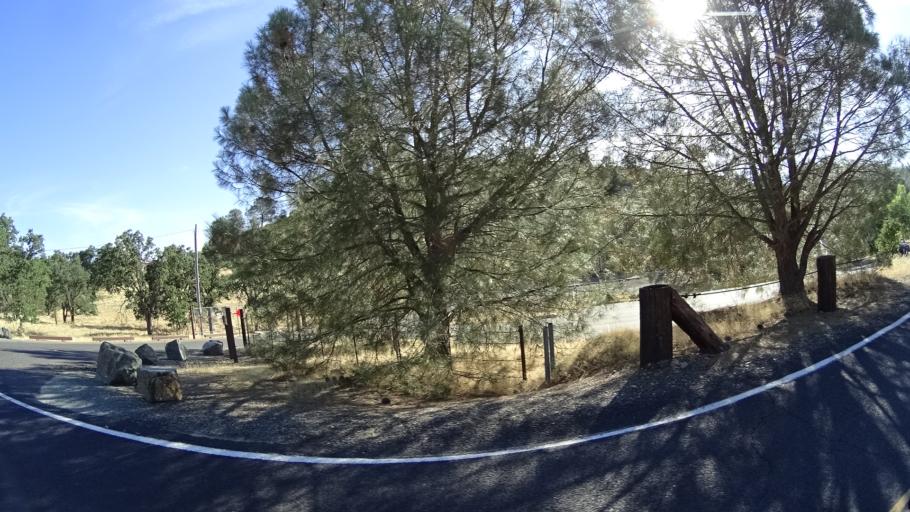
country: US
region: California
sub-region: Calaveras County
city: Valley Springs
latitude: 38.1826
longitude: -120.7948
